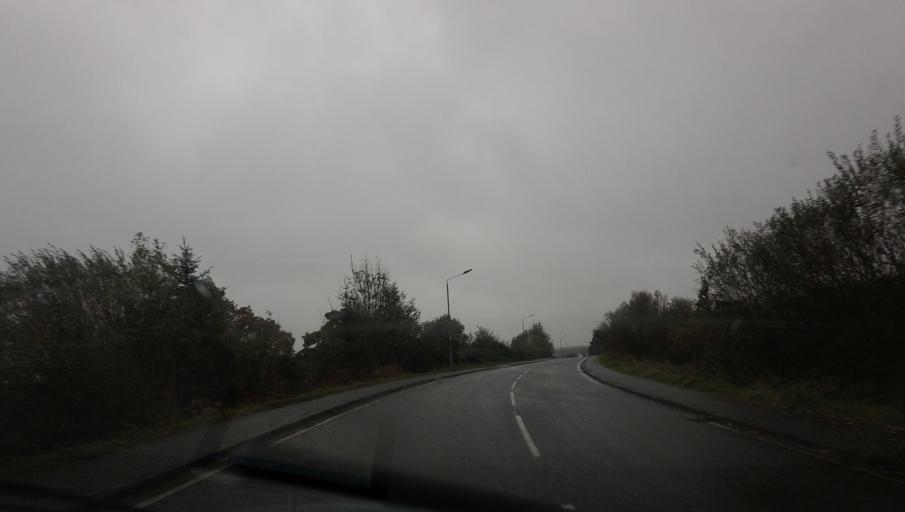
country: GB
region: Scotland
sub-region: Argyll and Bute
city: Isle Of Mull
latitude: 56.6171
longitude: -6.0719
